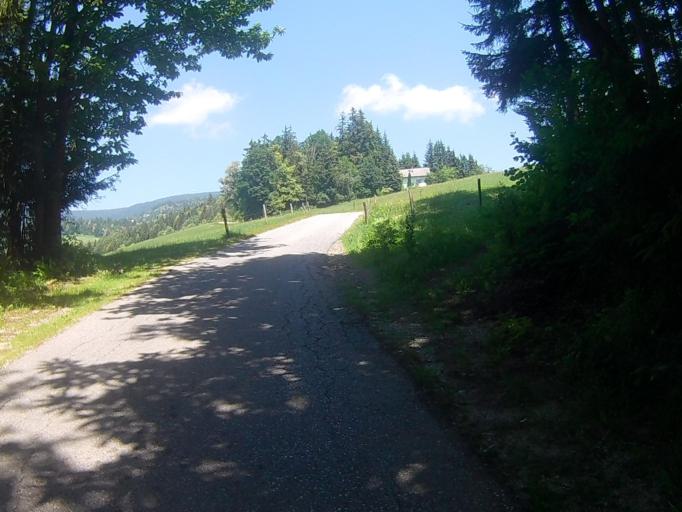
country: SI
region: Race-Fram
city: Morje
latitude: 46.4768
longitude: 15.5881
